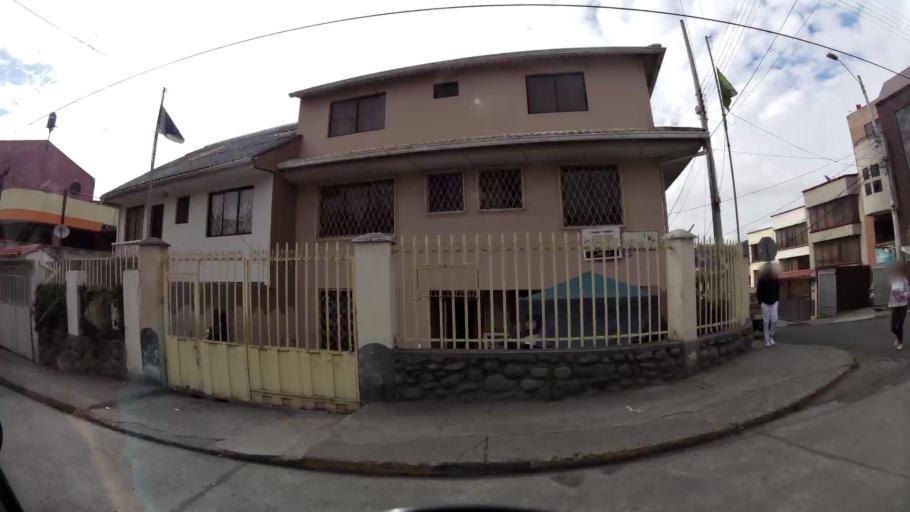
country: EC
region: Azuay
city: Cuenca
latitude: -2.8935
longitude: -78.9765
